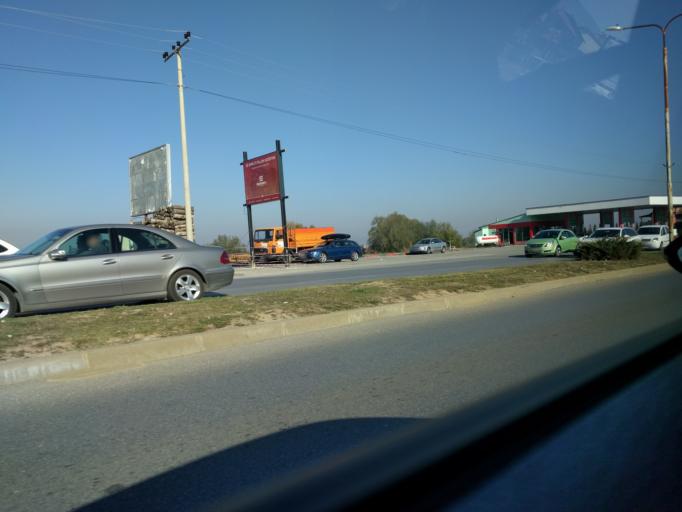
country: XK
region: Prizren
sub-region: Prizren
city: Prizren
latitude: 42.2298
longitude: 20.7550
